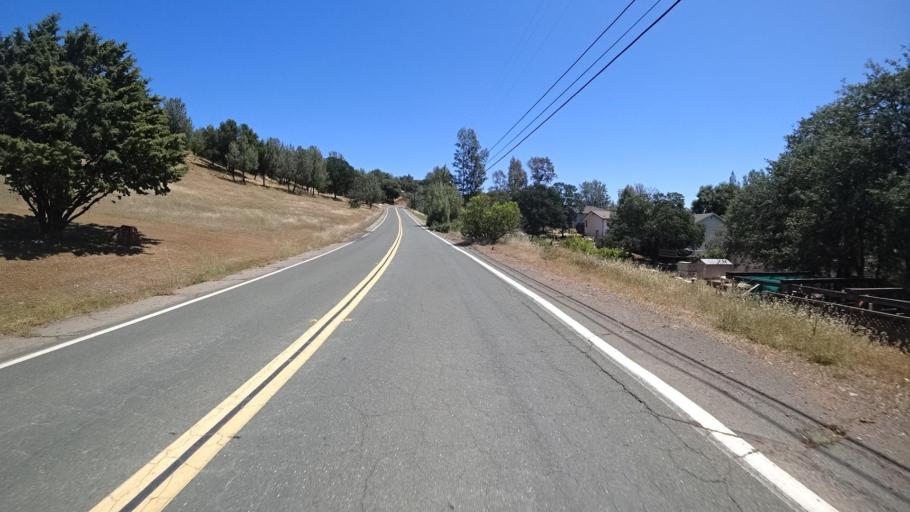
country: US
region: California
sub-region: Lake County
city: Hidden Valley Lake
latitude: 38.8189
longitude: -122.5681
